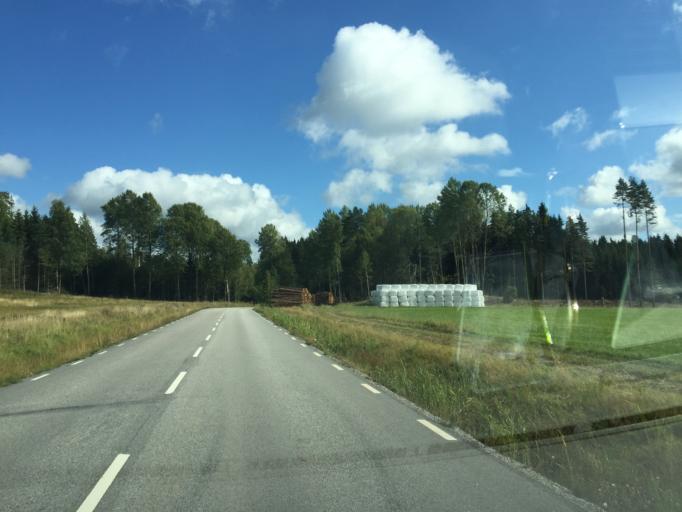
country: SE
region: Stockholm
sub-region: Botkyrka Kommun
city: Tullinge
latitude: 59.1669
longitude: 17.9016
